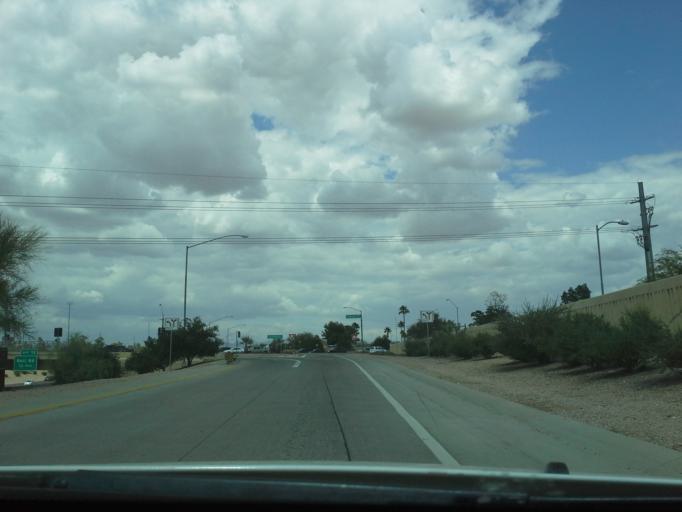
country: US
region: Arizona
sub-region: Maricopa County
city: Paradise Valley
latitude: 33.6251
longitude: -112.0067
